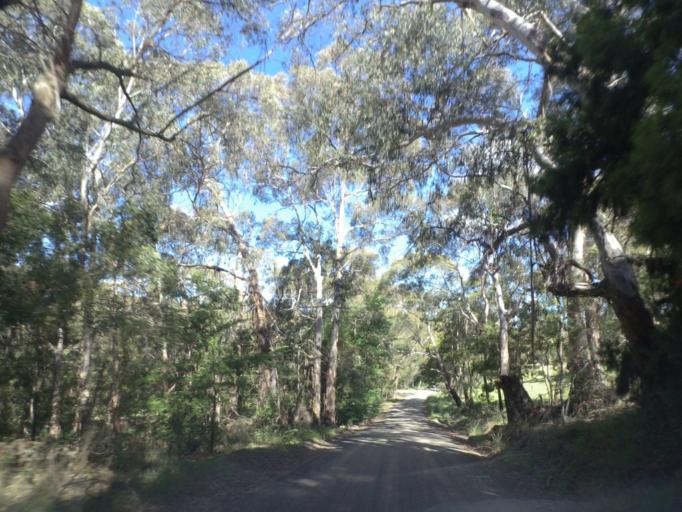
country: AU
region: Victoria
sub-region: Hume
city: Sunbury
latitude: -37.4263
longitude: 144.6497
